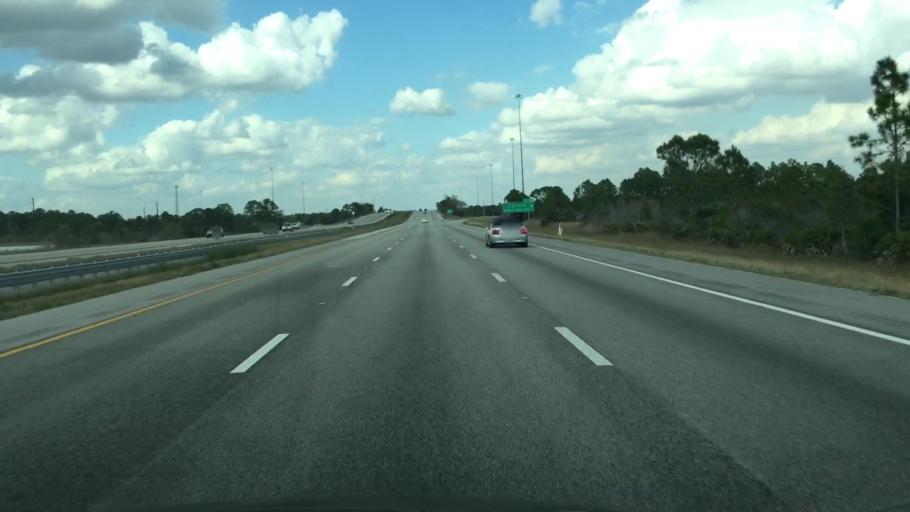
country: US
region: Florida
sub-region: Charlotte County
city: Charlotte Park
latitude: 26.8517
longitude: -81.9690
